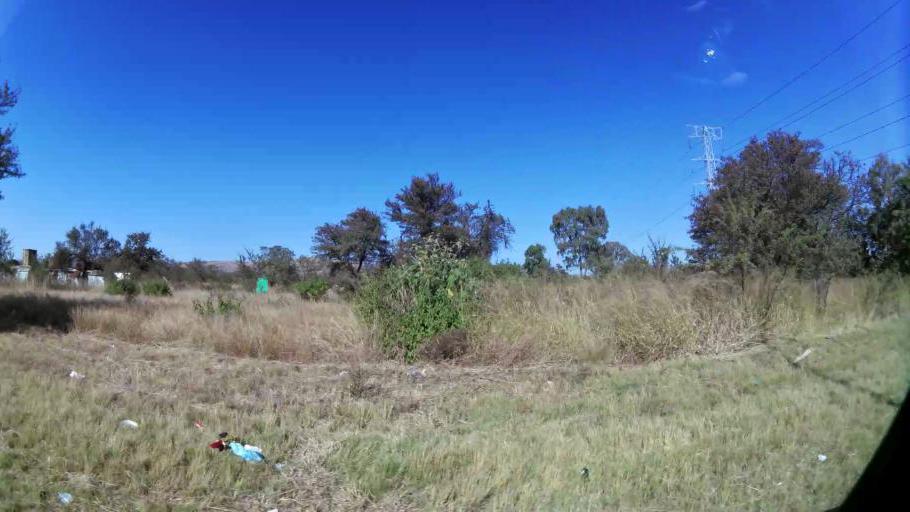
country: ZA
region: North-West
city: Ga-Rankuwa
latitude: -25.6608
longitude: 28.0819
